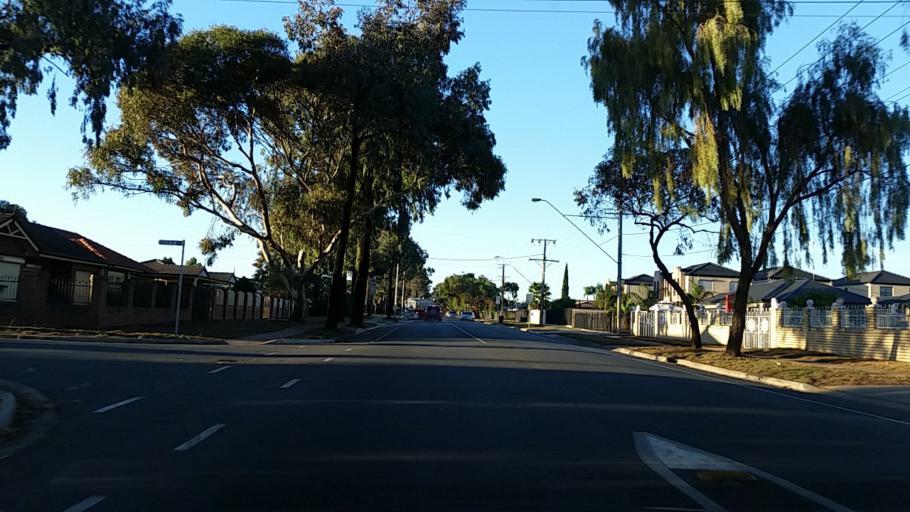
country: AU
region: South Australia
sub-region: Salisbury
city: Salisbury
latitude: -34.7659
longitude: 138.6541
